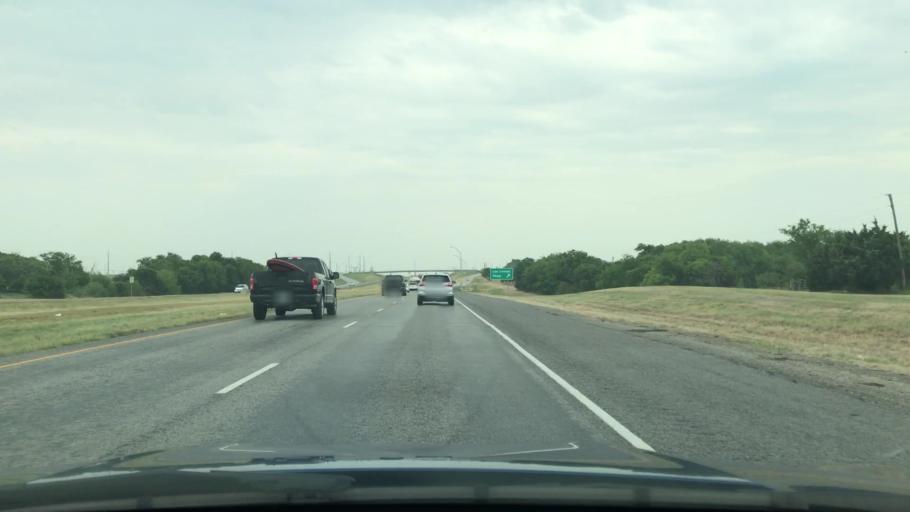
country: US
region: Texas
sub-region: Kaufman County
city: Talty
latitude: 32.7349
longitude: -96.3489
